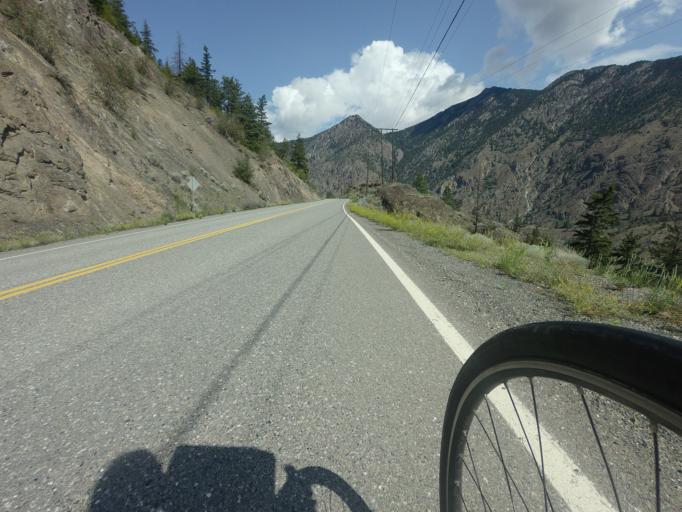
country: CA
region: British Columbia
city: Lillooet
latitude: 50.7517
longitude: -121.8934
